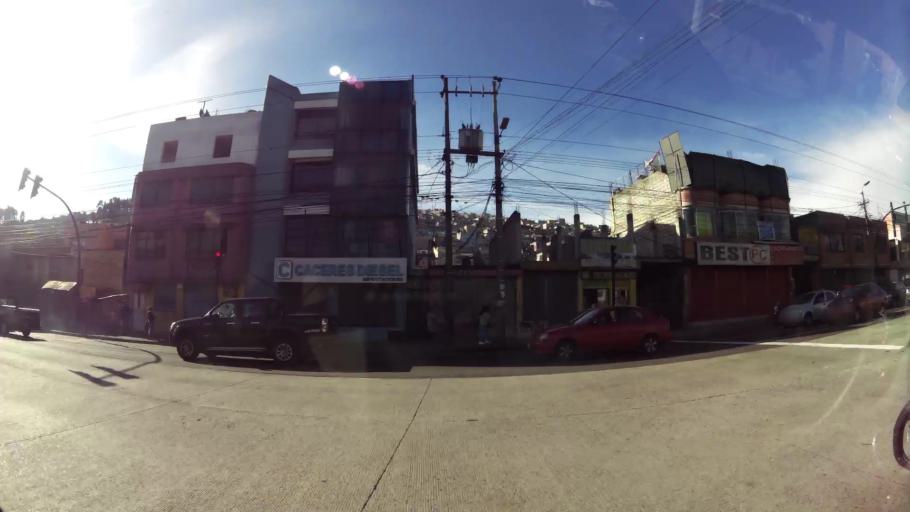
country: EC
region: Pichincha
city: Quito
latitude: -0.2818
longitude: -78.5344
